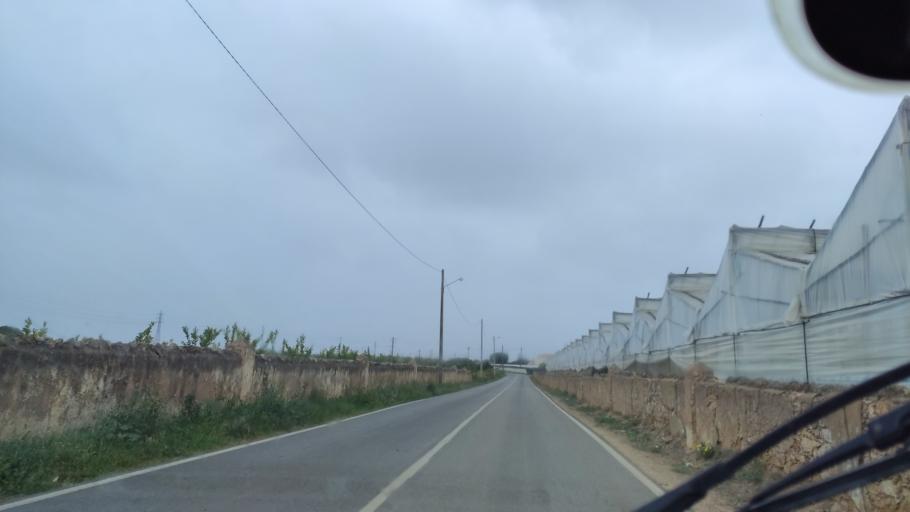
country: PT
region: Faro
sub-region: Faro
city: Santa Barbara de Nexe
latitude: 37.0734
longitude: -7.9425
